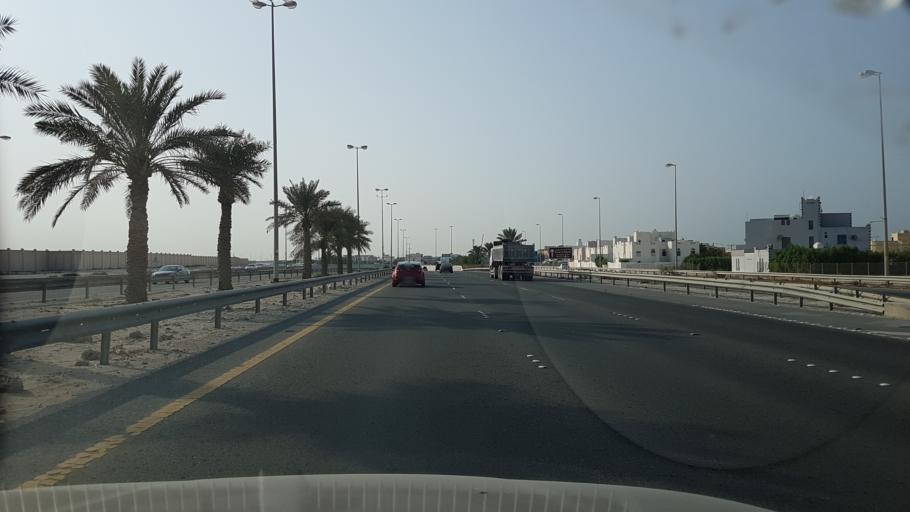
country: BH
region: Central Governorate
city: Madinat Hamad
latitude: 26.1035
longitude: 50.5112
